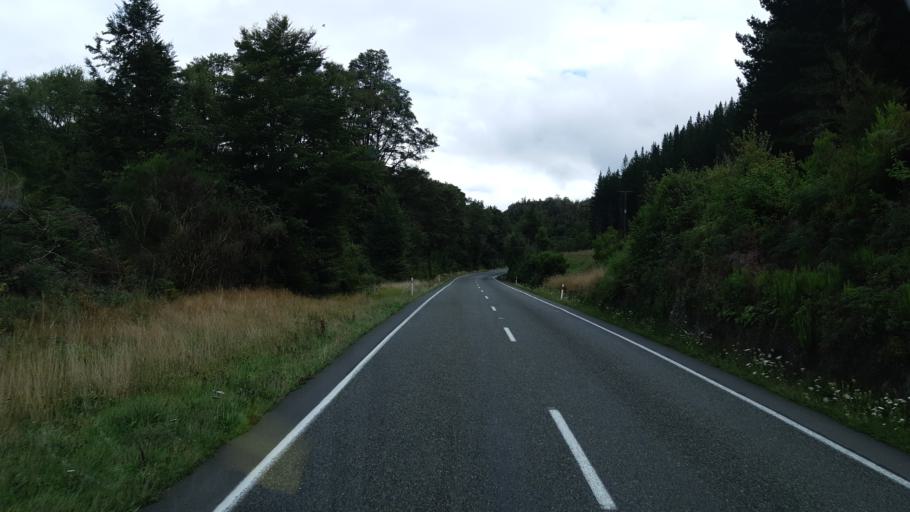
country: NZ
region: West Coast
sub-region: Buller District
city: Westport
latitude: -41.8263
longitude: 172.2391
